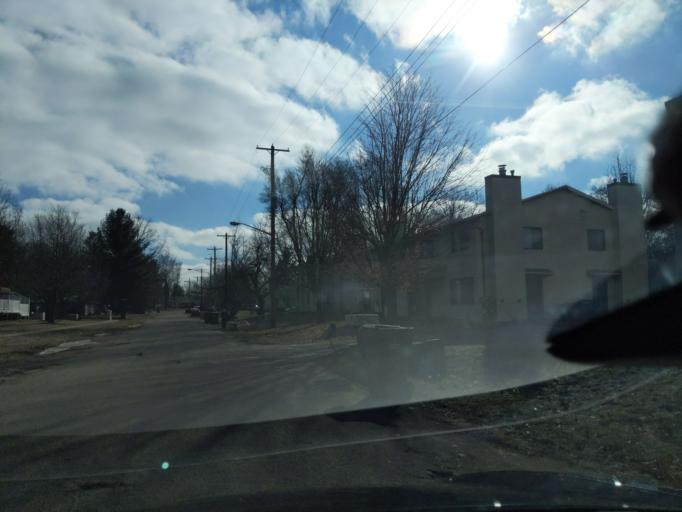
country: US
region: Michigan
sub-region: Ingham County
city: Lansing
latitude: 42.6746
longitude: -84.5761
